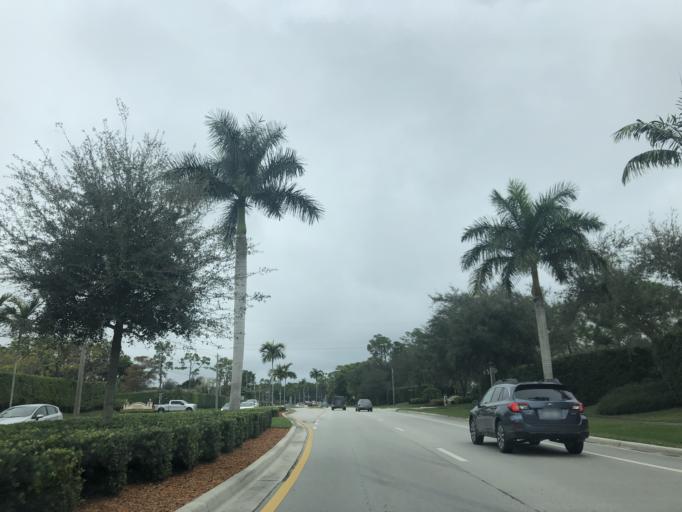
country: US
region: Florida
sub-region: Palm Beach County
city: Wellington
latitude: 26.6692
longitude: -80.2461
